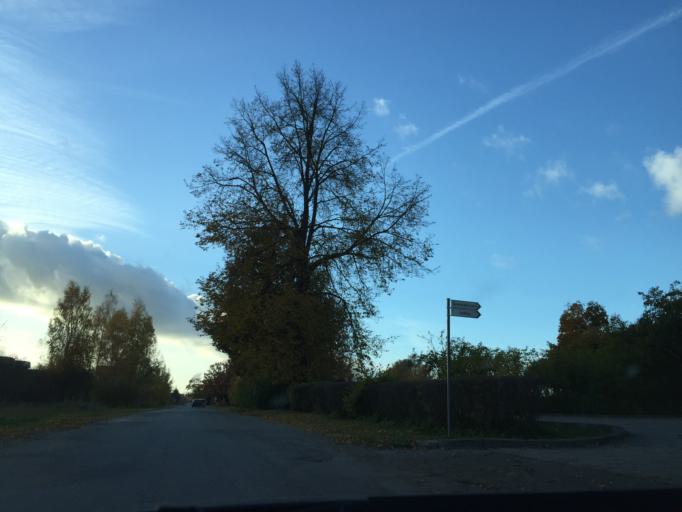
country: LV
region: Ogre
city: Jumprava
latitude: 56.7673
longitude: 25.0049
